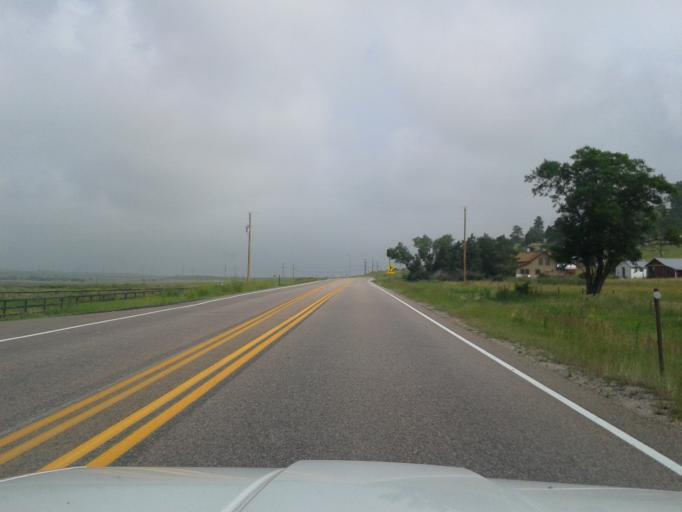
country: US
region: Colorado
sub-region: Elbert County
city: Elizabeth
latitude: 39.2575
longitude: -104.7021
